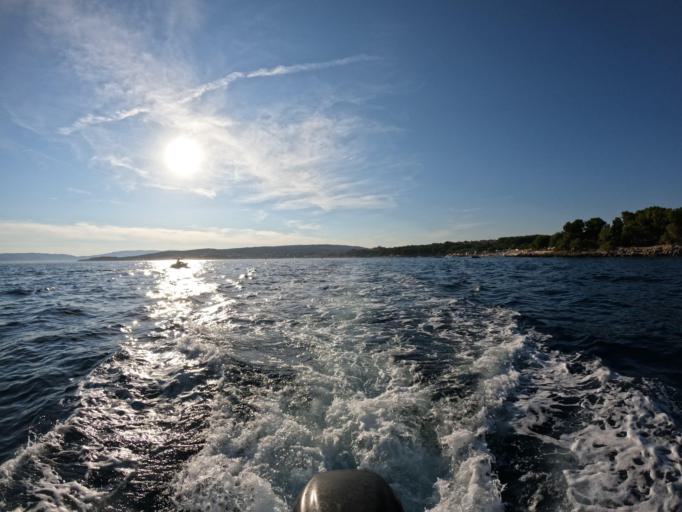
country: HR
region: Primorsko-Goranska
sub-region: Grad Krk
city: Krk
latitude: 45.0192
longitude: 14.5931
